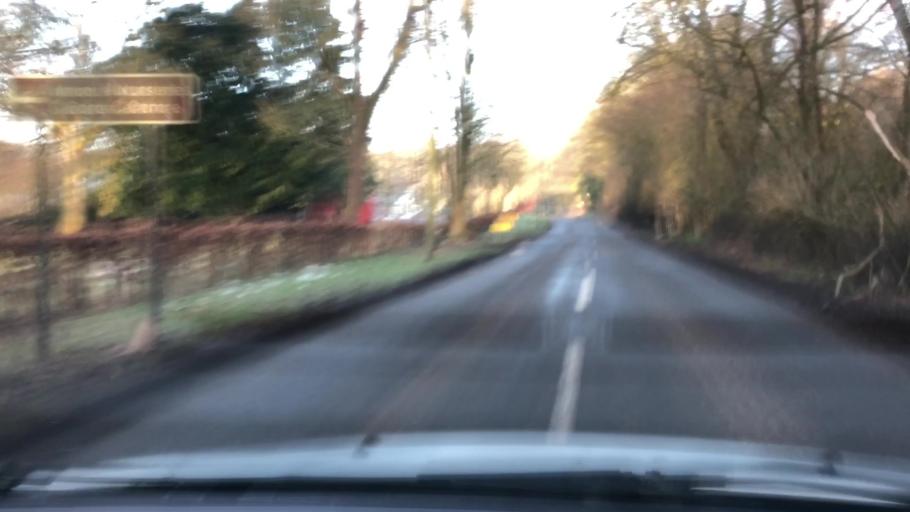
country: GB
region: England
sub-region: Hampshire
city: Alton
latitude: 51.1900
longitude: -1.0086
